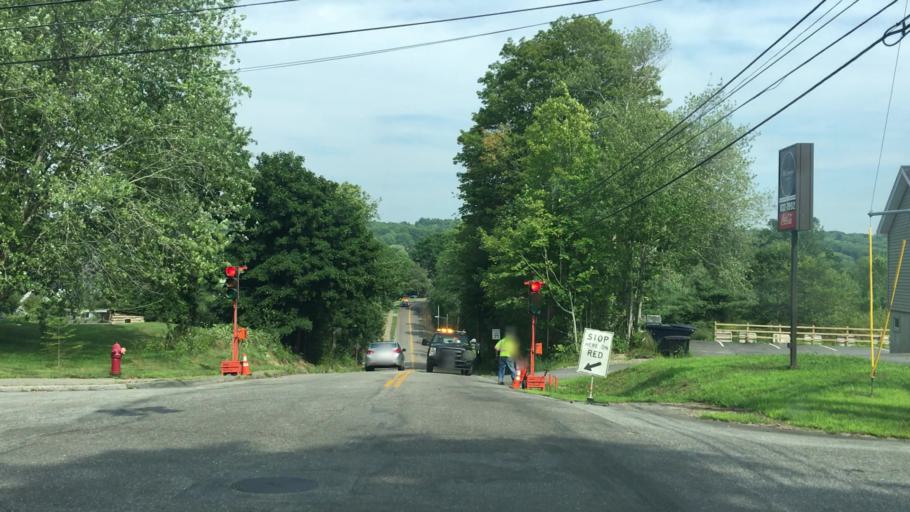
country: US
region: Maine
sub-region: Lincoln County
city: Waldoboro
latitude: 44.0957
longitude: -69.3845
